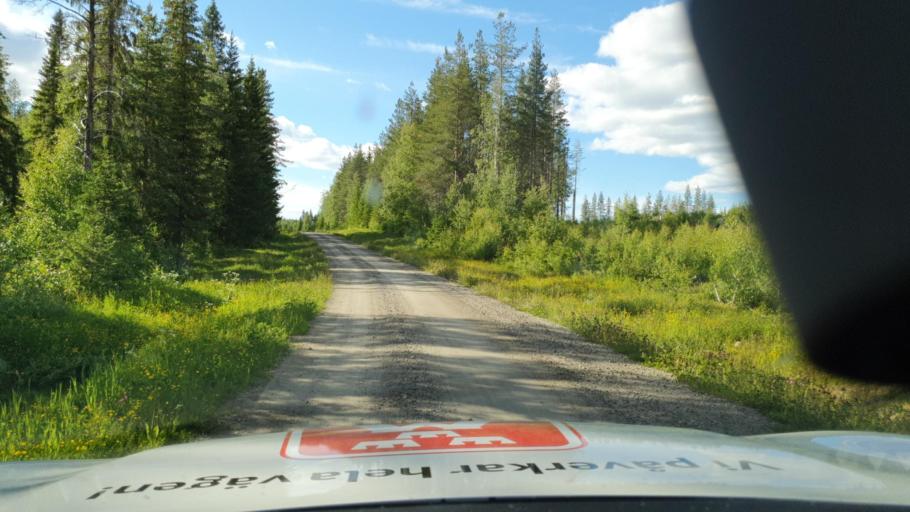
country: SE
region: Vaesterbotten
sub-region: Lycksele Kommun
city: Lycksele
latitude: 64.4825
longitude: 18.2841
